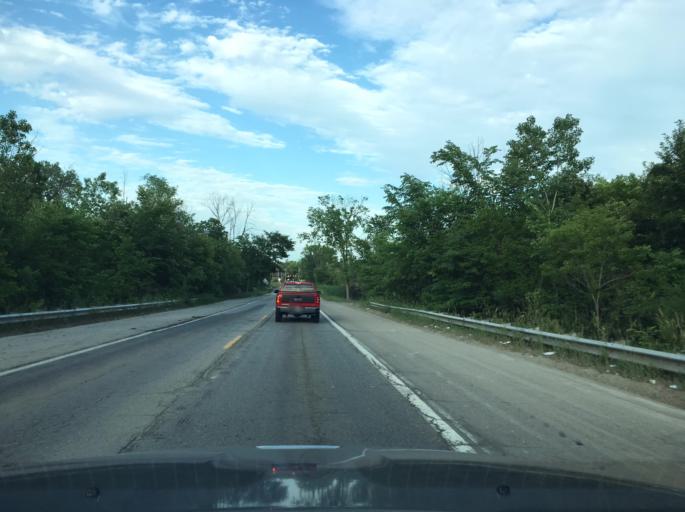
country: US
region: Michigan
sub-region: Macomb County
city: New Haven
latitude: 42.7177
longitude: -82.8815
